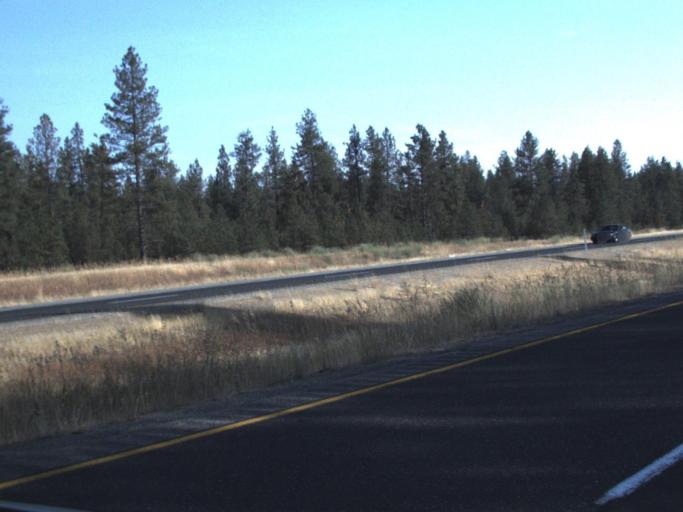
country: US
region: Washington
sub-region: Spokane County
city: Mead
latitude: 47.8778
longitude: -117.3578
